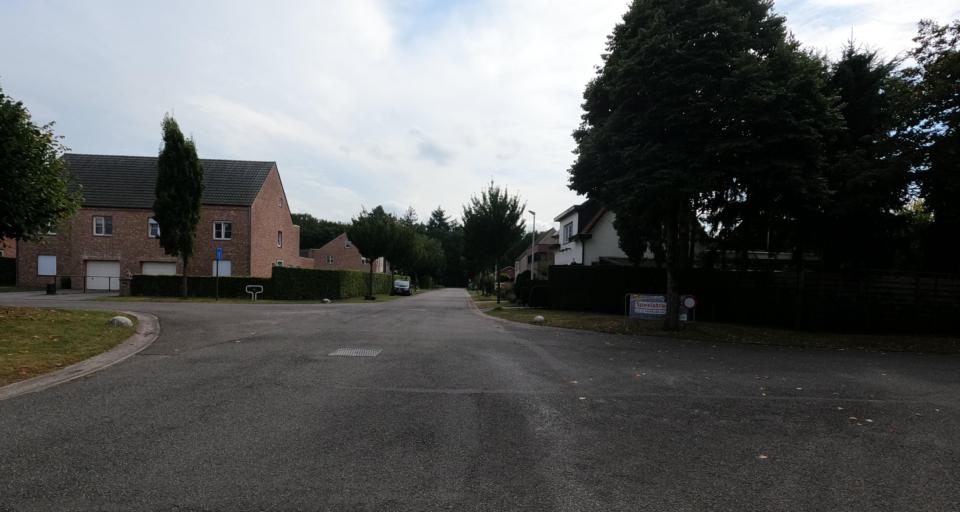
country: BE
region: Flanders
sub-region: Provincie Antwerpen
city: Kalmthout
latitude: 51.4236
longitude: 4.4592
